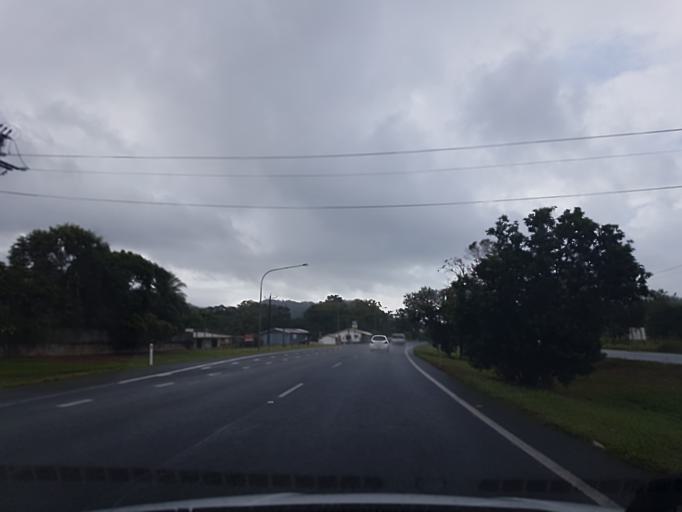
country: AU
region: Queensland
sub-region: Cairns
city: Yorkeys Knob
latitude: -16.8274
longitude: 145.6923
